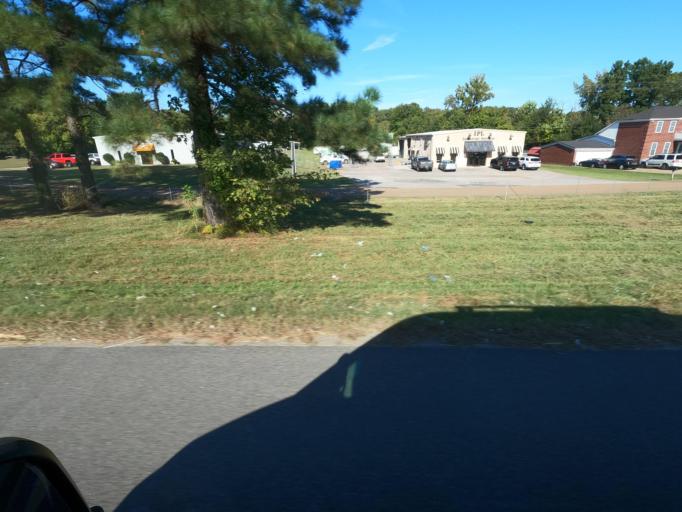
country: US
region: Tennessee
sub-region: Tipton County
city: Brighton
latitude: 35.4741
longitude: -89.7480
